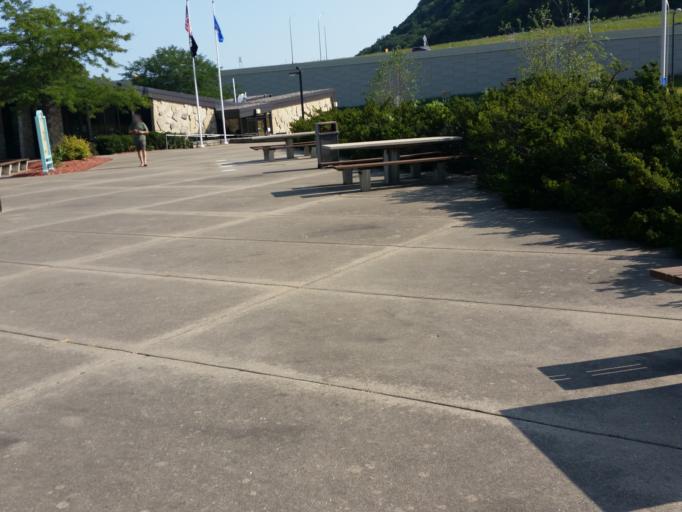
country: US
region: Minnesota
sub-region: Houston County
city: La Crescent
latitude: 43.8598
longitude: -91.3049
